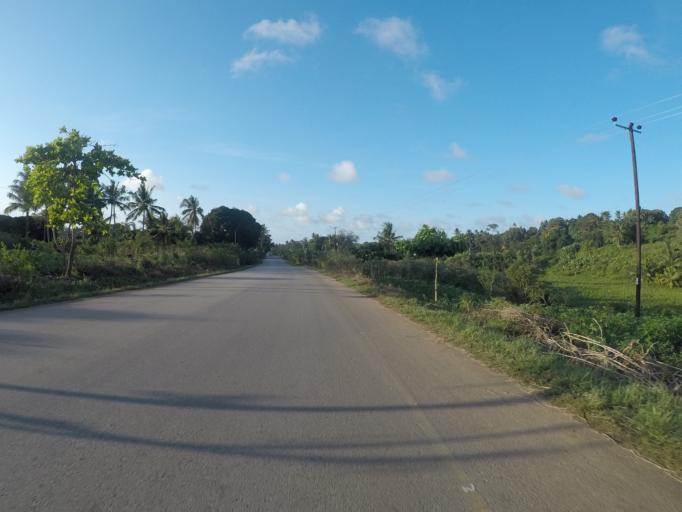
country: TZ
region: Zanzibar North
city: Kijini
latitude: -5.8318
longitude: 39.2914
